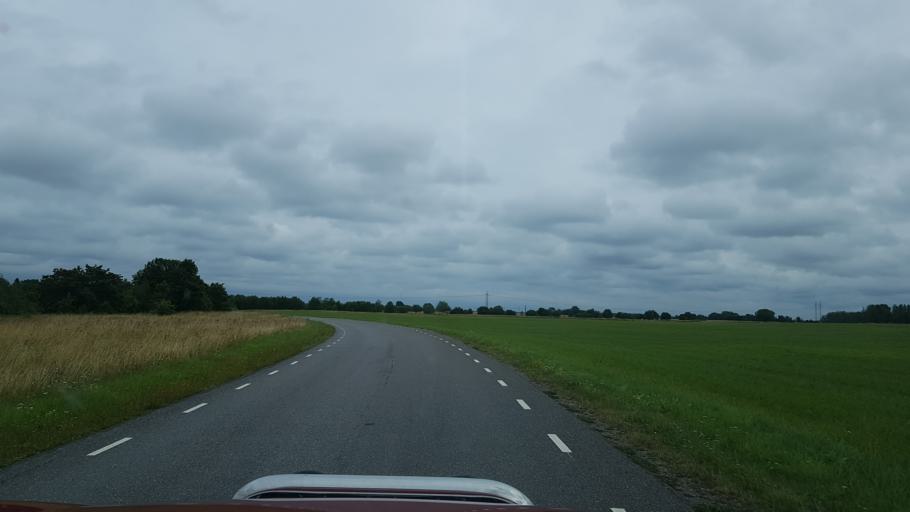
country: EE
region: Ida-Virumaa
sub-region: Puessi linn
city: Pussi
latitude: 59.4000
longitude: 27.0113
